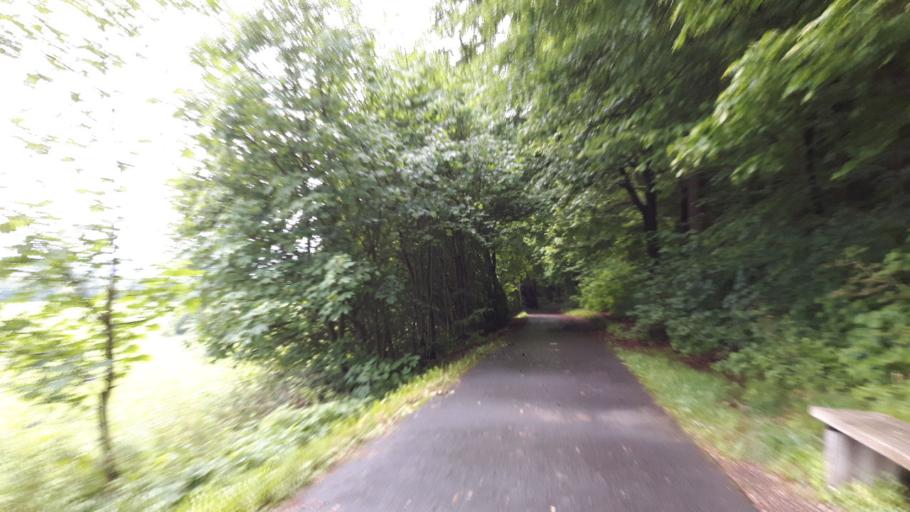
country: DE
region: Thuringia
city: Veilsdorf
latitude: 50.4087
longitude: 10.7915
